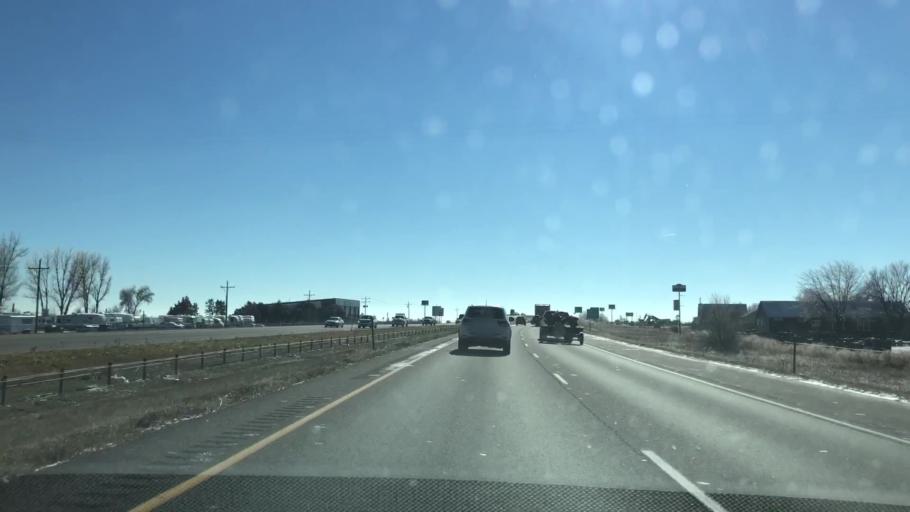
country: US
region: Colorado
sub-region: Weld County
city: Johnstown
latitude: 40.3551
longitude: -104.9821
